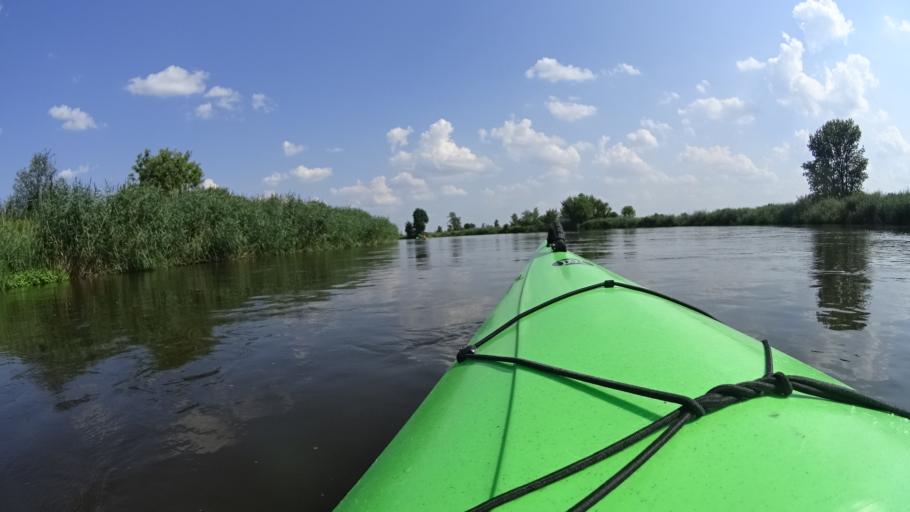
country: PL
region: Masovian Voivodeship
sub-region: Powiat bialobrzeski
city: Wysmierzyce
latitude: 51.6560
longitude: 20.8413
